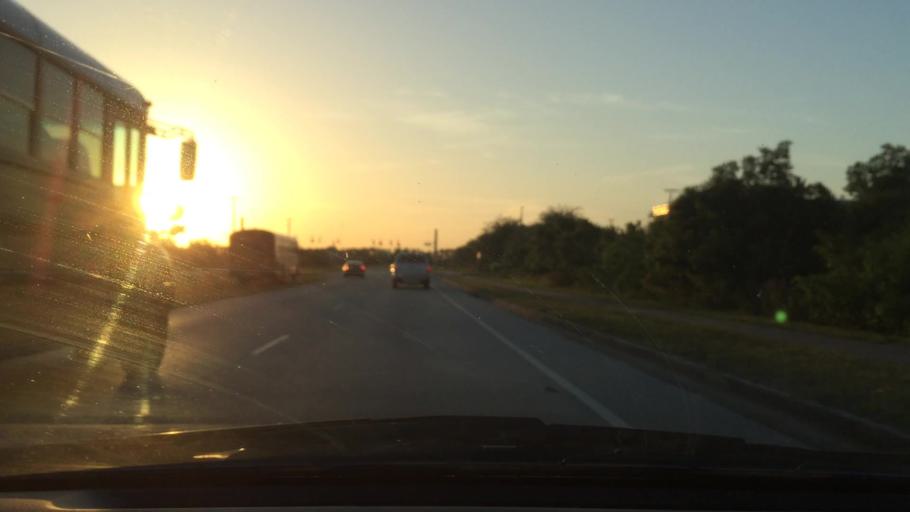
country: US
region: Florida
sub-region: Hillsborough County
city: Progress Village
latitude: 27.9153
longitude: -82.3455
